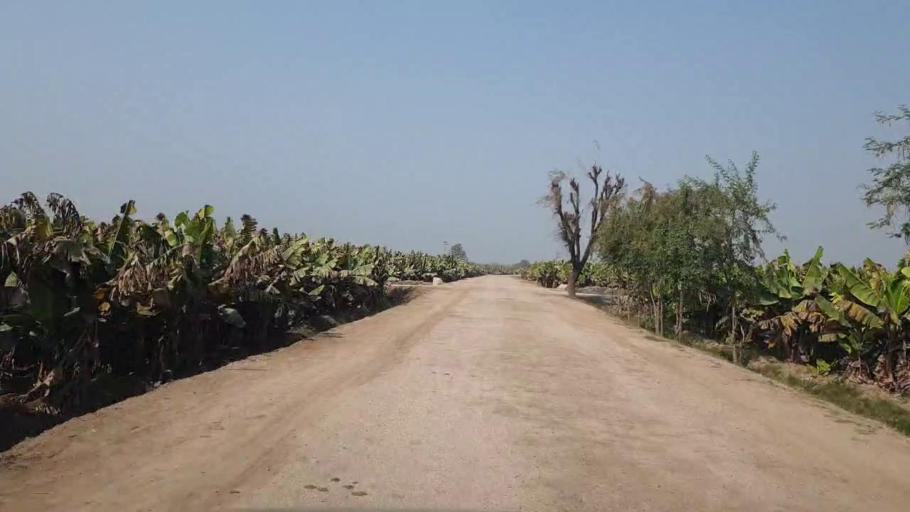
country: PK
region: Sindh
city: Bhit Shah
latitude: 25.7935
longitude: 68.4993
